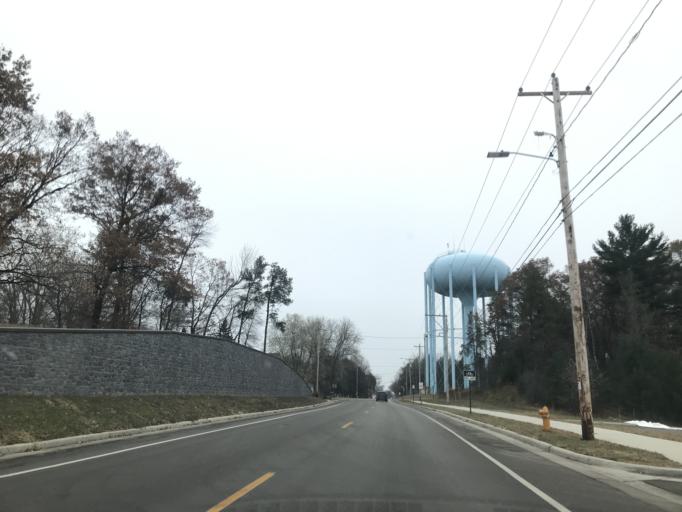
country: US
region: Wisconsin
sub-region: Marinette County
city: Marinette
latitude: 45.0792
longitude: -87.6297
